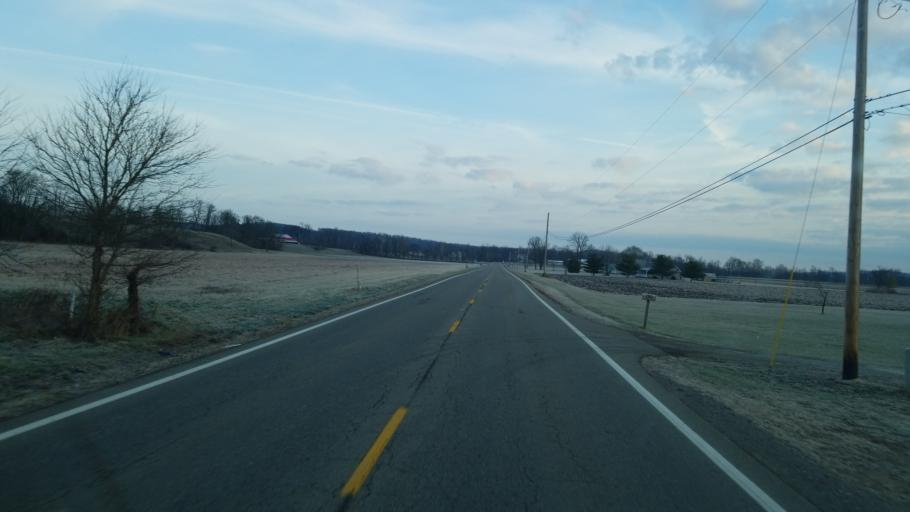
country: US
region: Ohio
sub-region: Ross County
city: Frankfort
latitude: 39.2716
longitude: -83.1675
